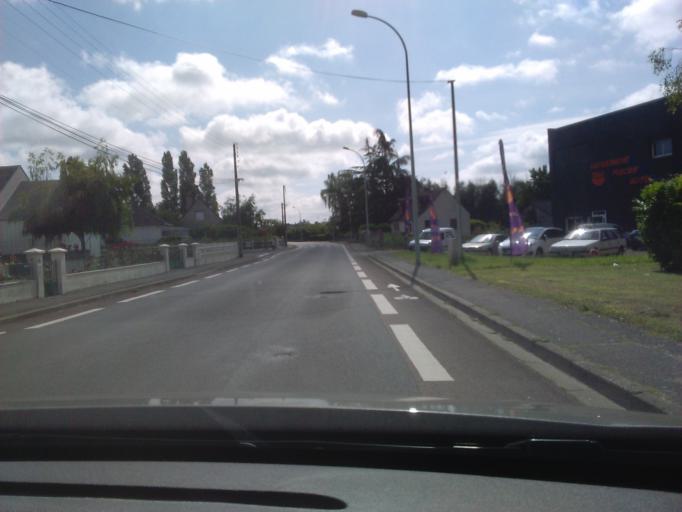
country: FR
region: Centre
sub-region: Departement du Loir-et-Cher
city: Vendome
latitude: 47.8024
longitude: 1.0511
